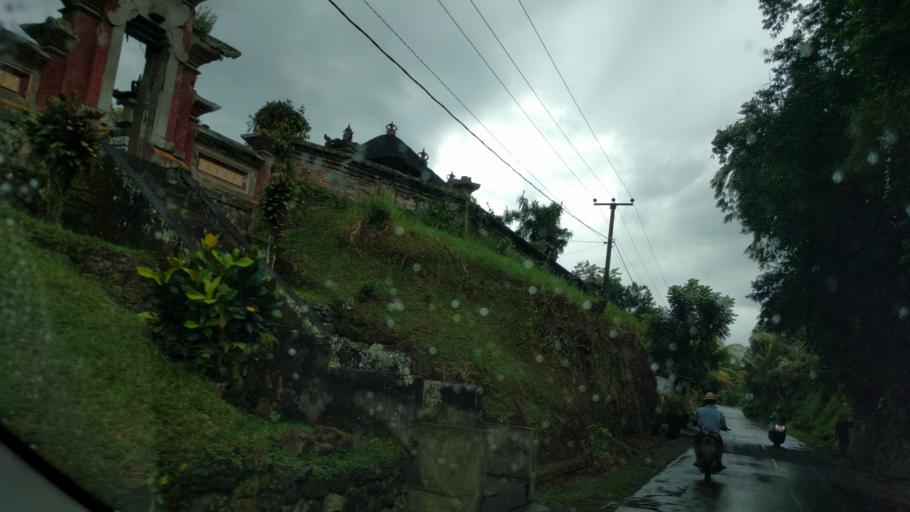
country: ID
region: Bali
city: Bunutan
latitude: -8.4733
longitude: 115.2598
